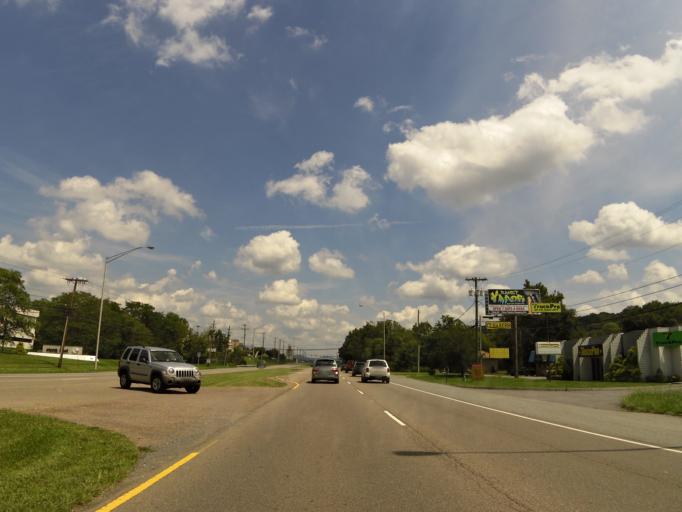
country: US
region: Tennessee
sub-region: Sullivan County
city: Bloomingdale
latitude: 36.5480
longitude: -82.4981
